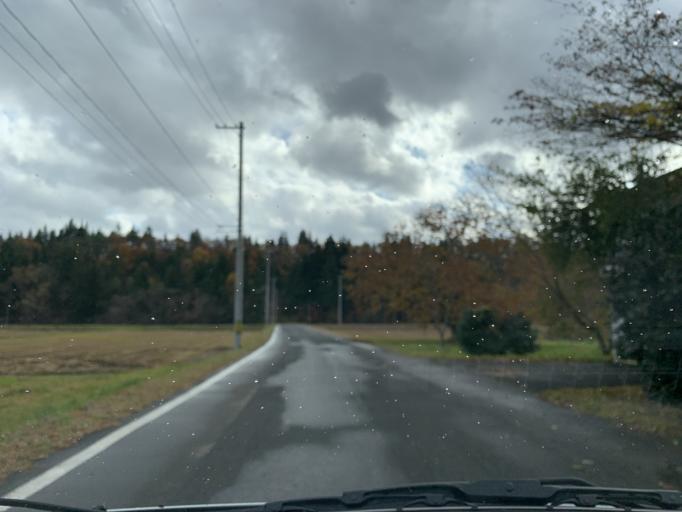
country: JP
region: Iwate
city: Mizusawa
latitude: 39.1193
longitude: 140.9581
